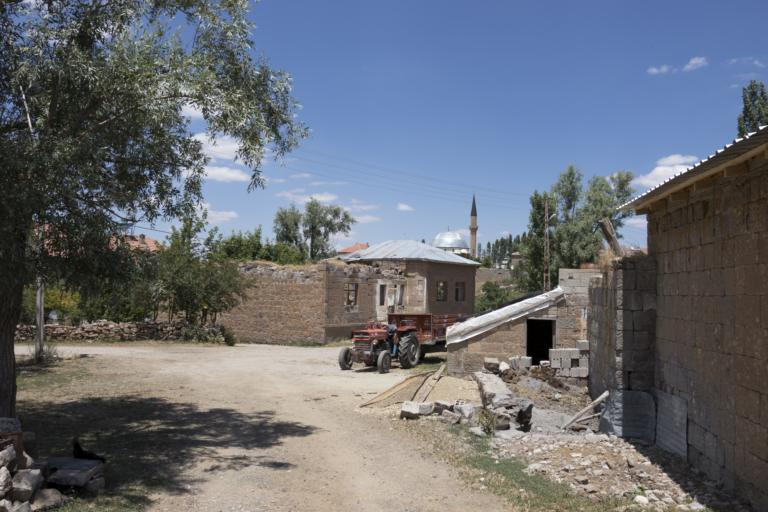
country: TR
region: Kayseri
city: Toklar
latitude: 38.4048
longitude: 36.0824
